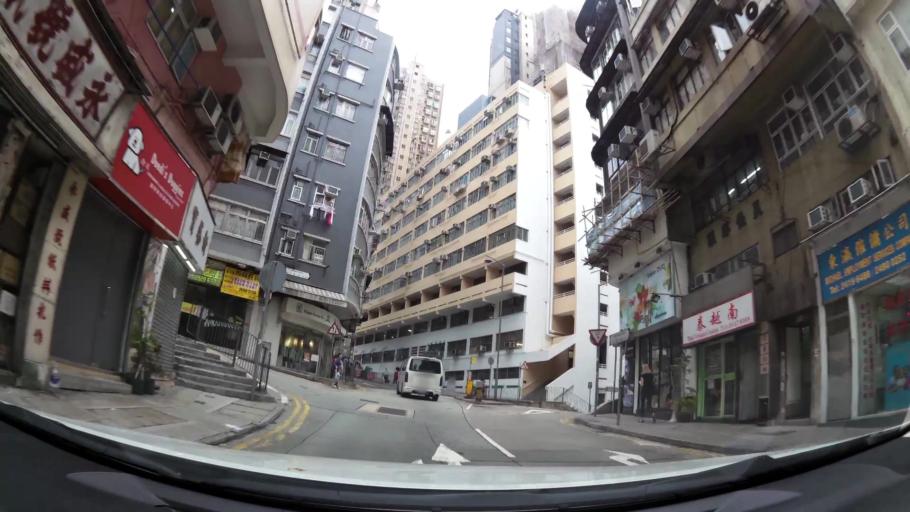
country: HK
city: Hong Kong
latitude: 22.2864
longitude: 114.1402
